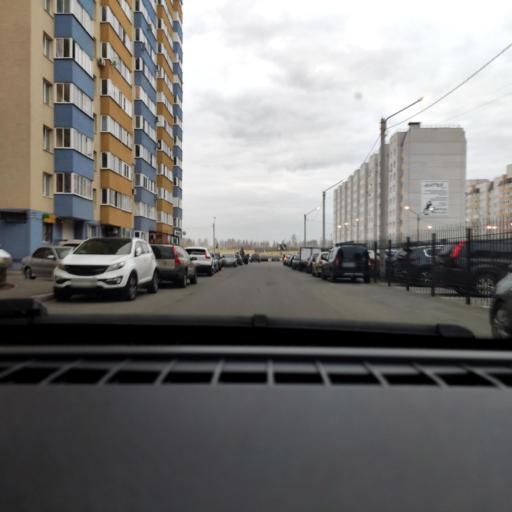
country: RU
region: Voronezj
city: Somovo
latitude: 51.7411
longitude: 39.3137
